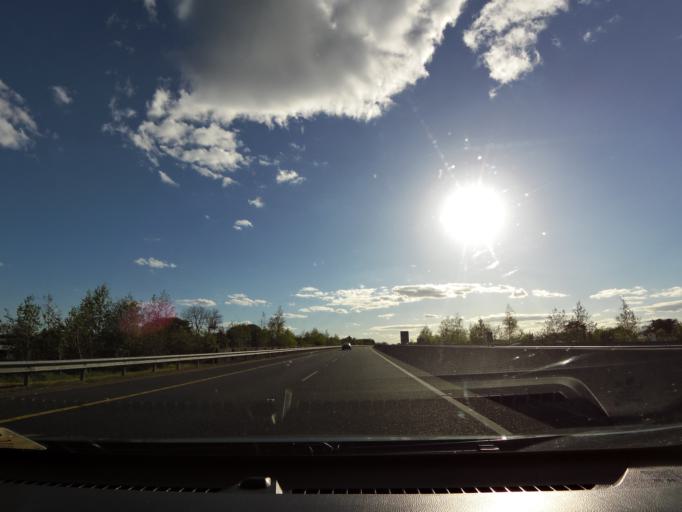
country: IE
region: Connaught
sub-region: County Galway
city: Ballinasloe
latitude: 53.3121
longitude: -8.2567
